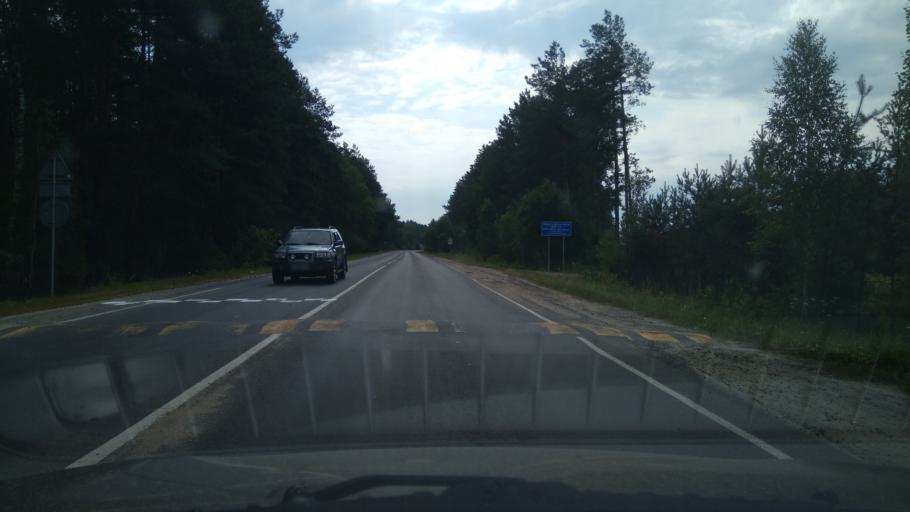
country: BY
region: Brest
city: Nyakhachava
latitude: 52.5875
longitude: 25.0936
